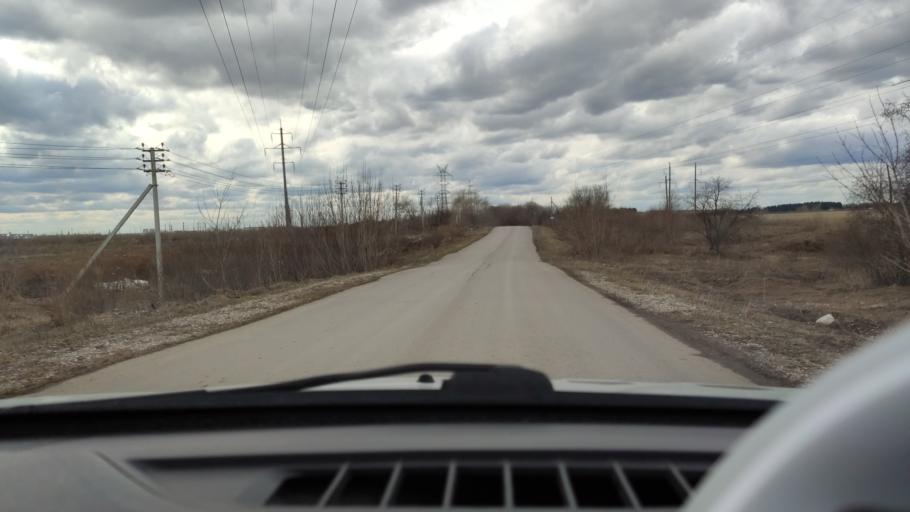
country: RU
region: Perm
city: Froly
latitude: 57.9282
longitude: 56.2612
